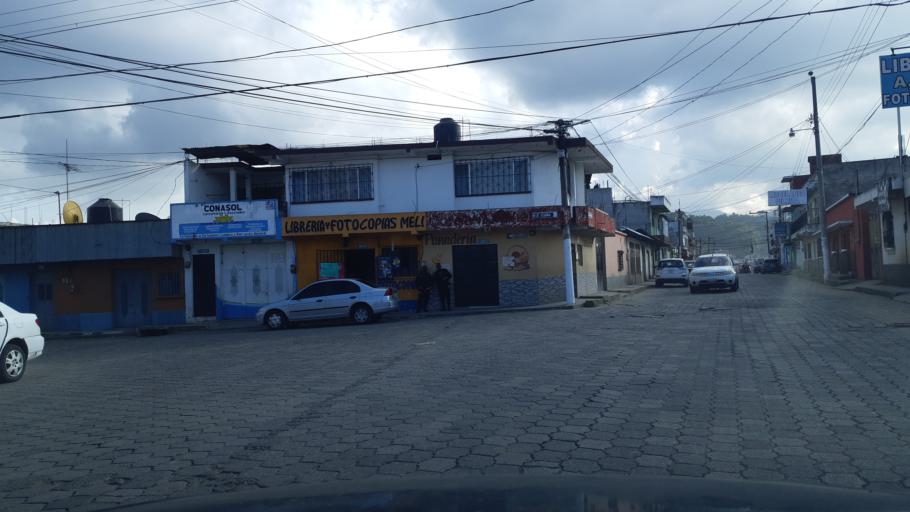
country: GT
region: Chimaltenango
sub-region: Municipio de Chimaltenango
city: Chimaltenango
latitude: 14.6606
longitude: -90.8282
